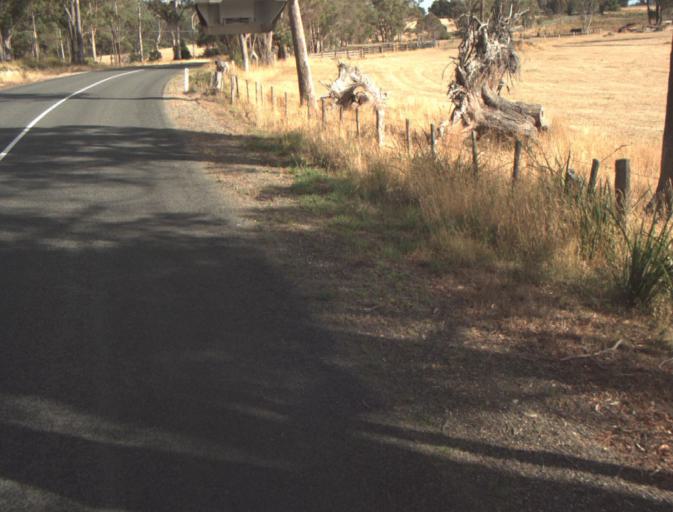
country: AU
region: Tasmania
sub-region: Dorset
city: Bridport
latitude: -41.1146
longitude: 147.2020
